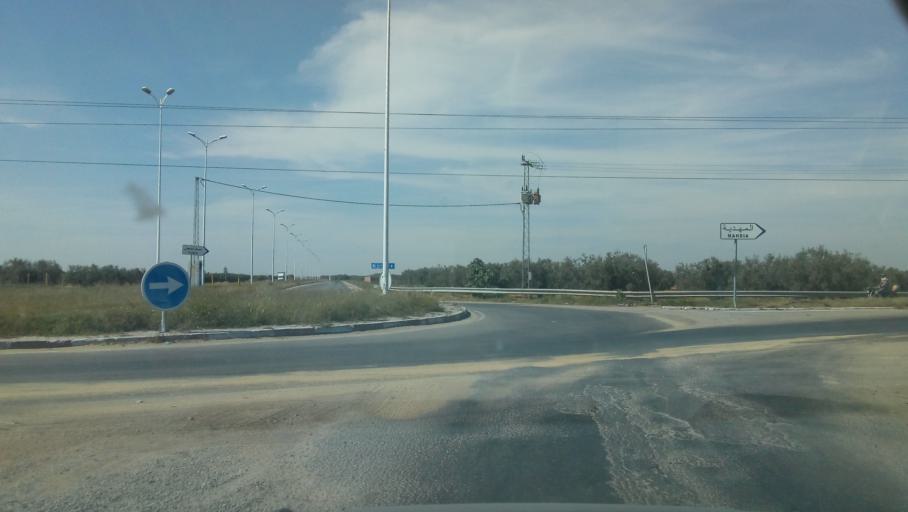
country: TN
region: Safaqis
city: Al Qarmadah
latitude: 34.8512
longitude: 10.8289
